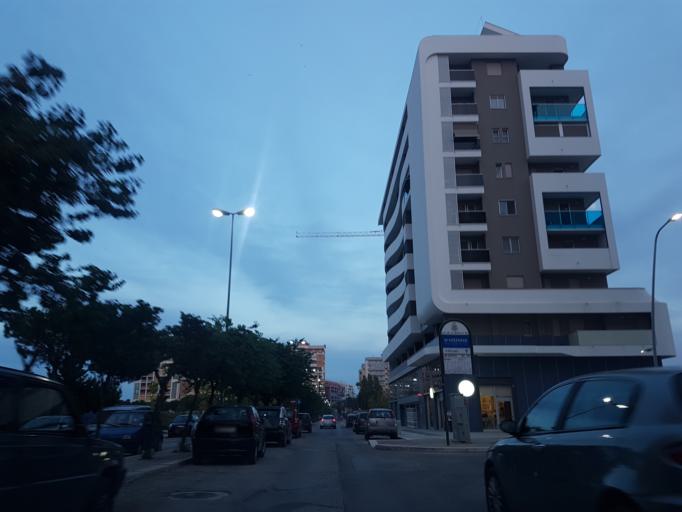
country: IT
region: Apulia
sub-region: Provincia di Barletta - Andria - Trani
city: Barletta
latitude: 41.3060
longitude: 16.2750
